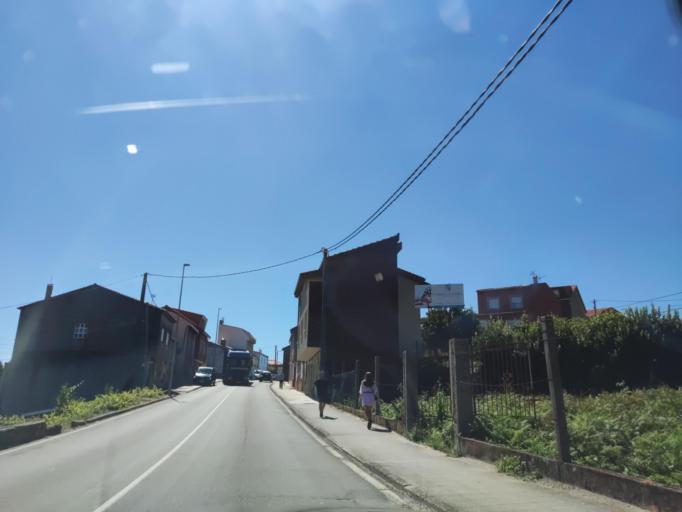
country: ES
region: Galicia
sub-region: Provincia da Coruna
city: Boiro
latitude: 42.6133
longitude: -8.9339
